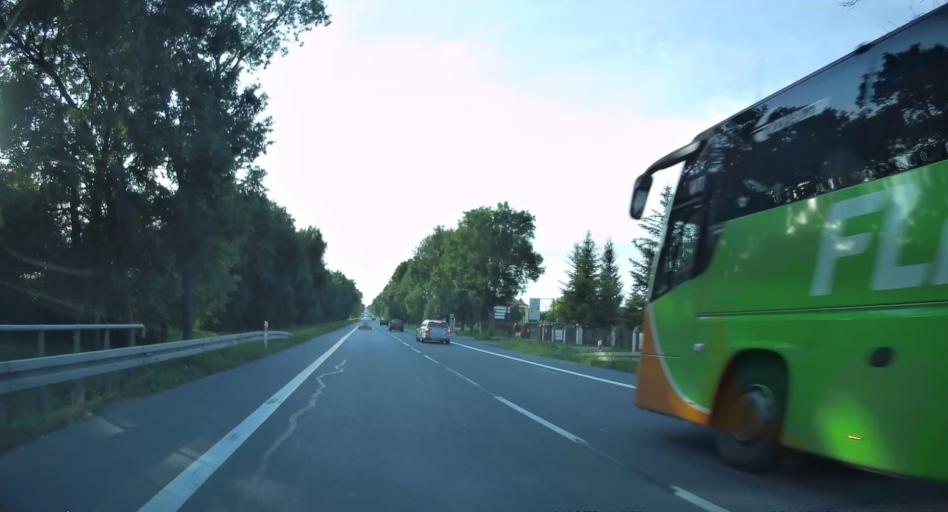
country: PL
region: Lesser Poland Voivodeship
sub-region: Powiat krakowski
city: Slomniki
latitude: 50.2549
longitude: 20.0857
